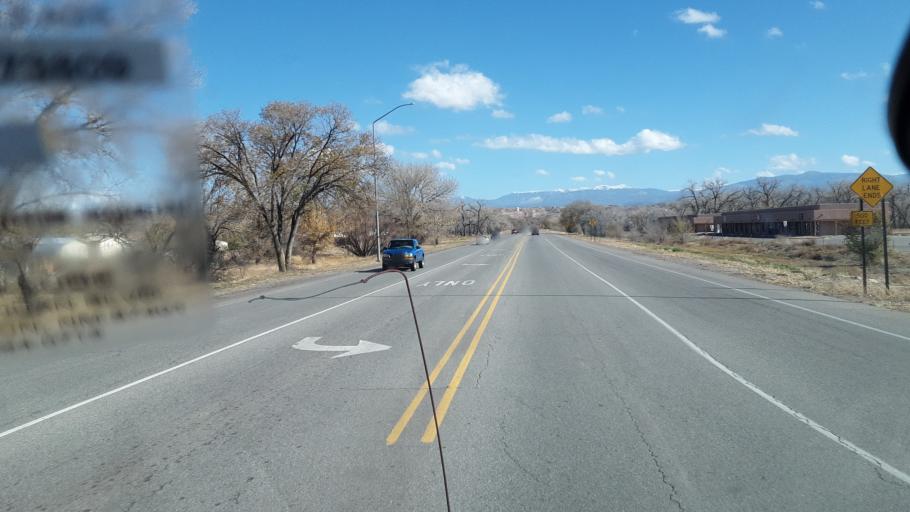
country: US
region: New Mexico
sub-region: Rio Arriba County
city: Espanola
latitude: 36.0082
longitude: -106.0801
